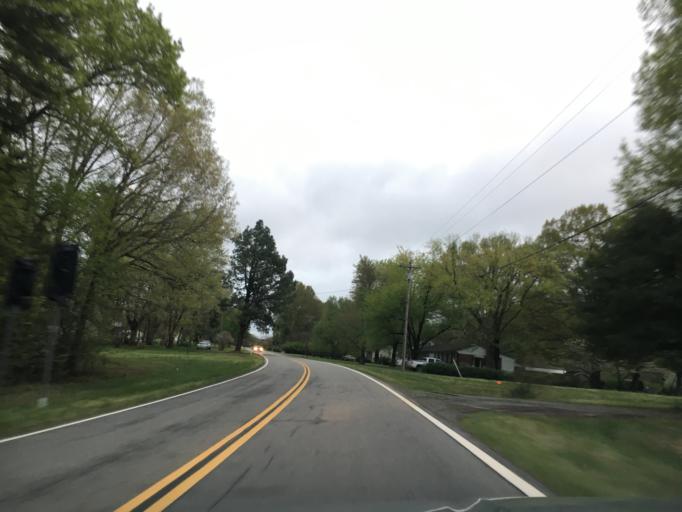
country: US
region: Virginia
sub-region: Halifax County
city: South Boston
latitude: 36.6612
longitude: -78.8808
